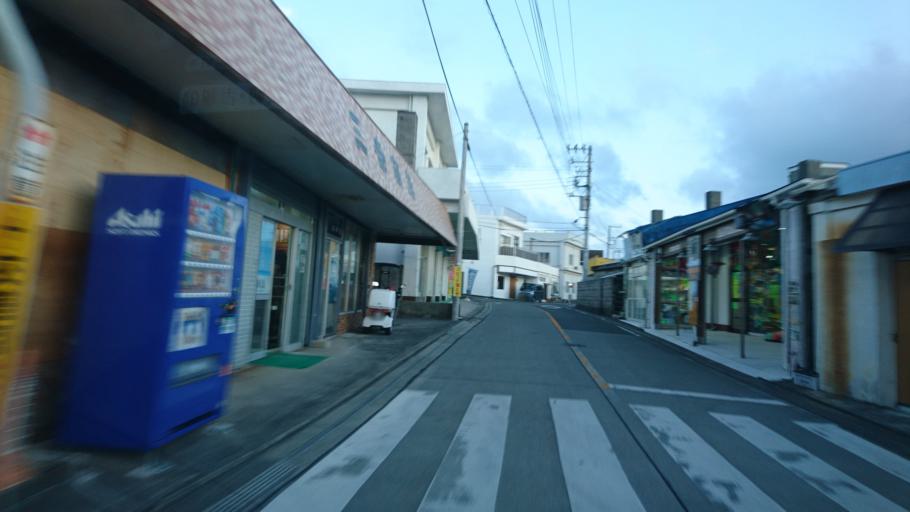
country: JP
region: Shizuoka
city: Shimoda
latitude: 34.3751
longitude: 139.2547
